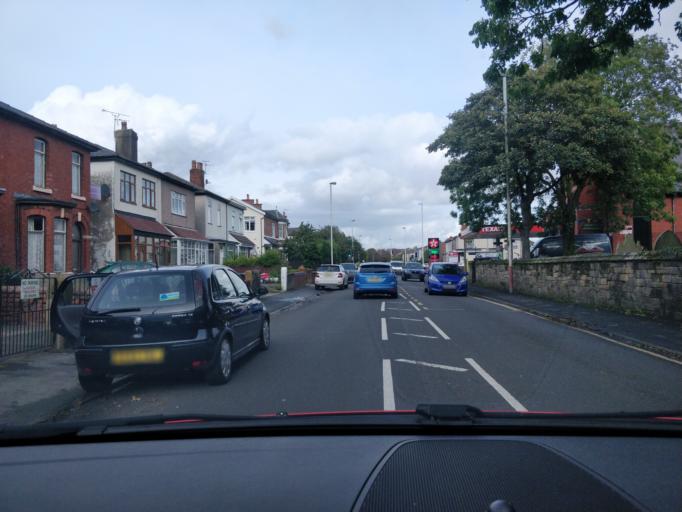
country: GB
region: England
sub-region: Sefton
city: Southport
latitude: 53.6365
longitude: -2.9980
